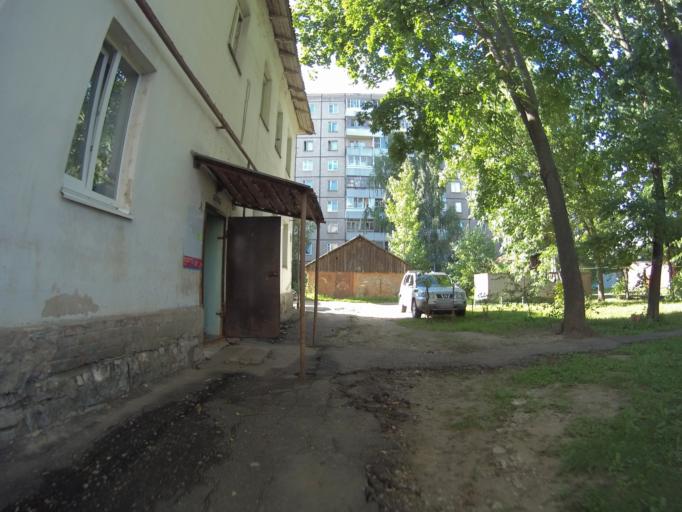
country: RU
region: Vladimir
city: Vladimir
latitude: 56.1491
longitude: 40.4297
